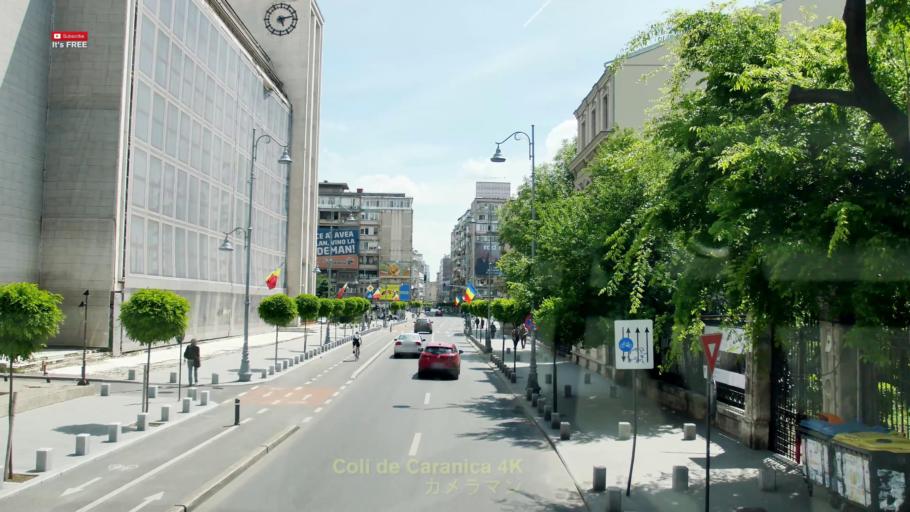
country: RO
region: Bucuresti
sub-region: Municipiul Bucuresti
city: Bucuresti
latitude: 44.4455
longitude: 26.0910
